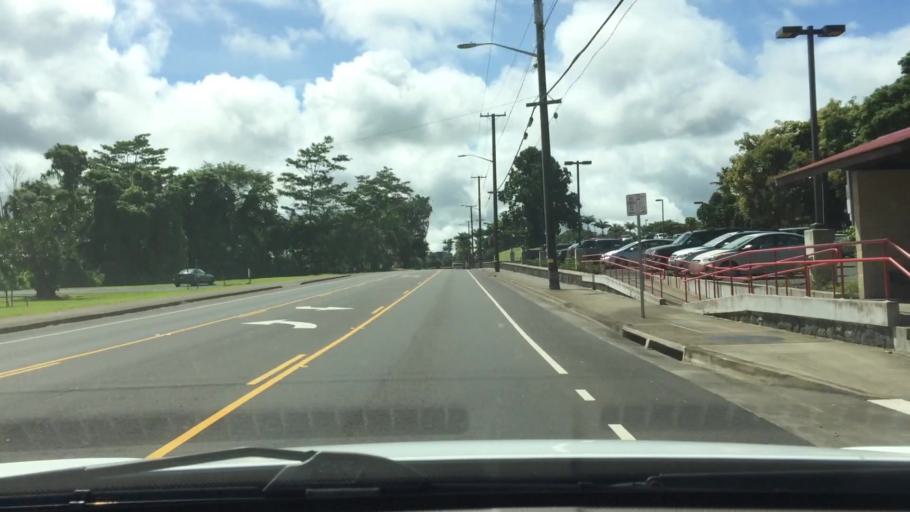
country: US
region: Hawaii
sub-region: Hawaii County
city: Hilo
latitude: 19.7037
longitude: -155.0790
